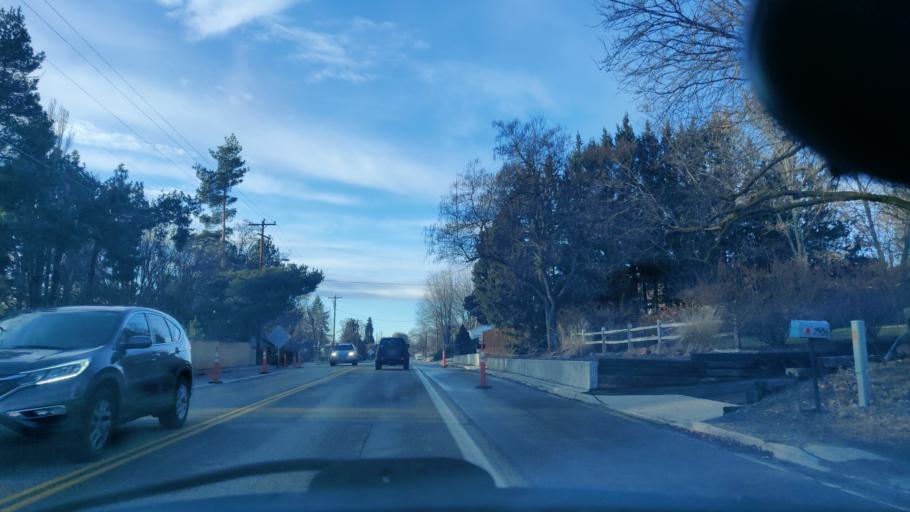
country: US
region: Idaho
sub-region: Ada County
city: Garden City
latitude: 43.6473
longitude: -116.2201
